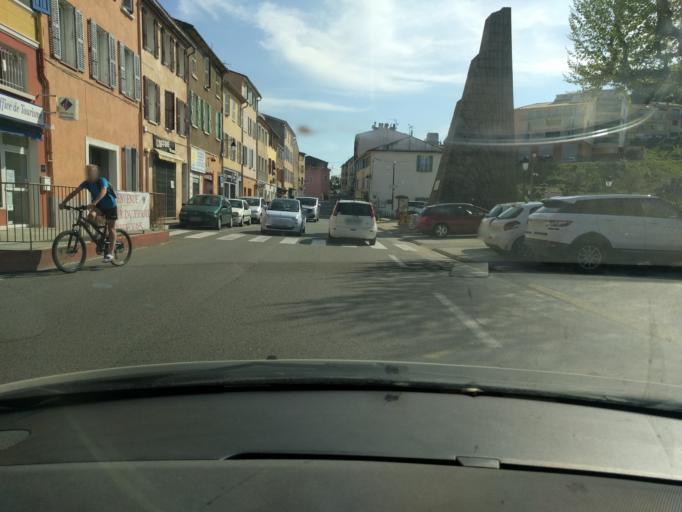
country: FR
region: Provence-Alpes-Cote d'Azur
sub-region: Departement du Var
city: Pierrefeu-du-Var
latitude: 43.2281
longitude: 6.1434
